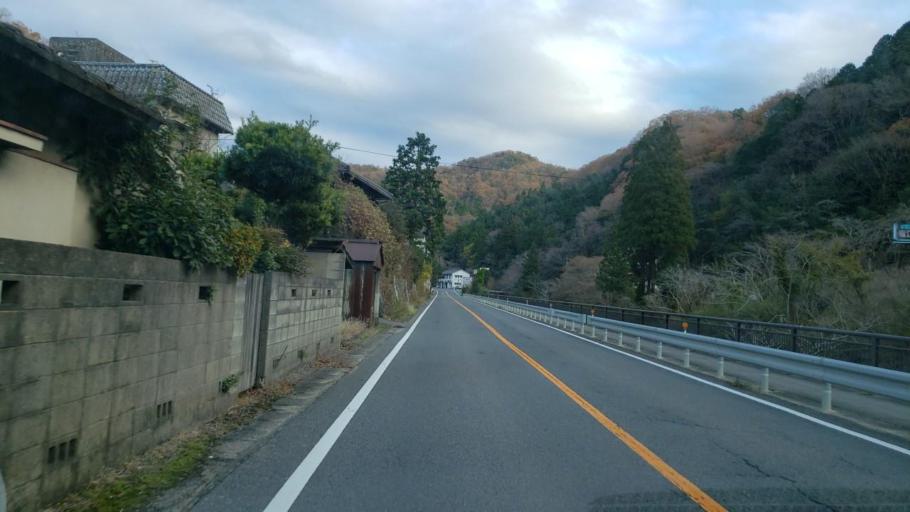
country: JP
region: Tokushima
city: Wakimachi
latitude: 34.1694
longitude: 134.0833
